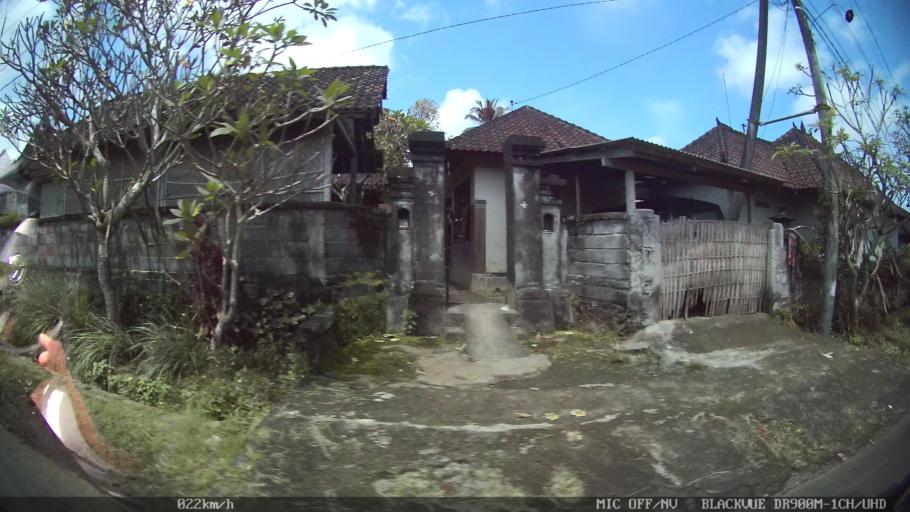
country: ID
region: Bali
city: Banjar Apuan Kaja
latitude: -8.5030
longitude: 115.3388
